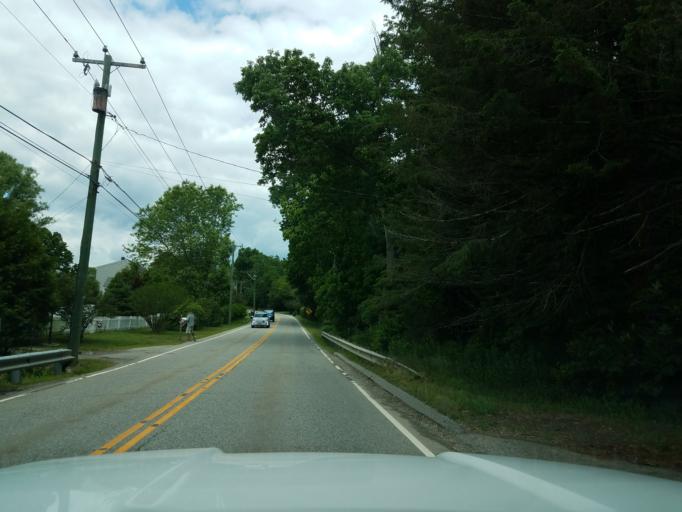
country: US
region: Connecticut
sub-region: Windham County
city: Wauregan
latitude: 41.7780
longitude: -71.9441
